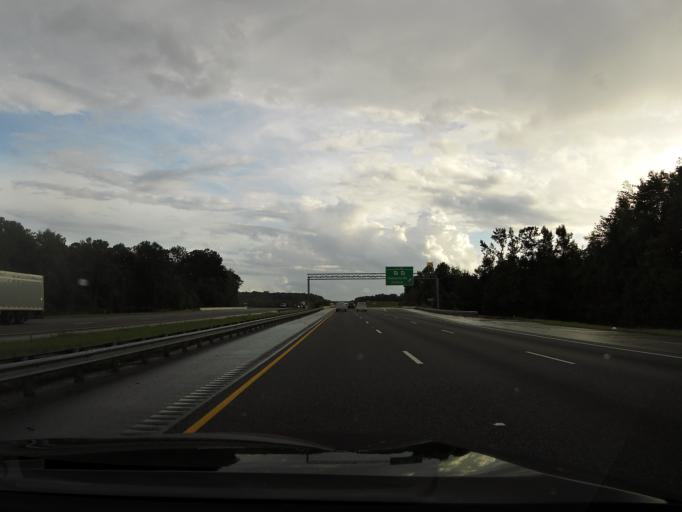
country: US
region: Georgia
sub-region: McIntosh County
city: Darien
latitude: 31.5377
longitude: -81.4452
